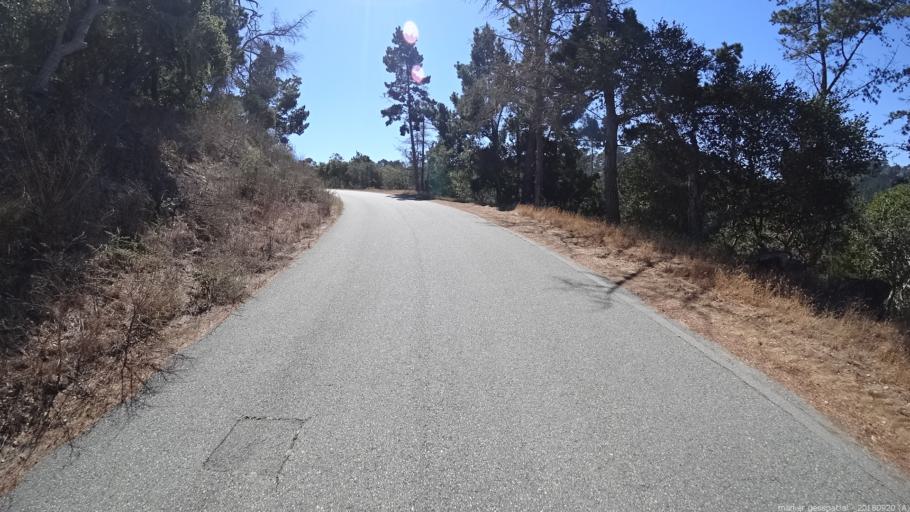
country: US
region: California
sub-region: Monterey County
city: Monterey
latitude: 36.5753
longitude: -121.8905
